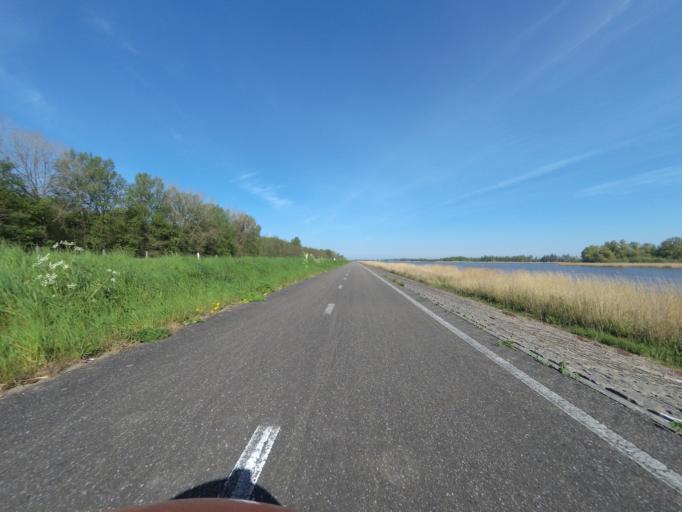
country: NL
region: Flevoland
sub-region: Gemeente Noordoostpolder
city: Ens
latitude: 52.5635
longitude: 5.8336
